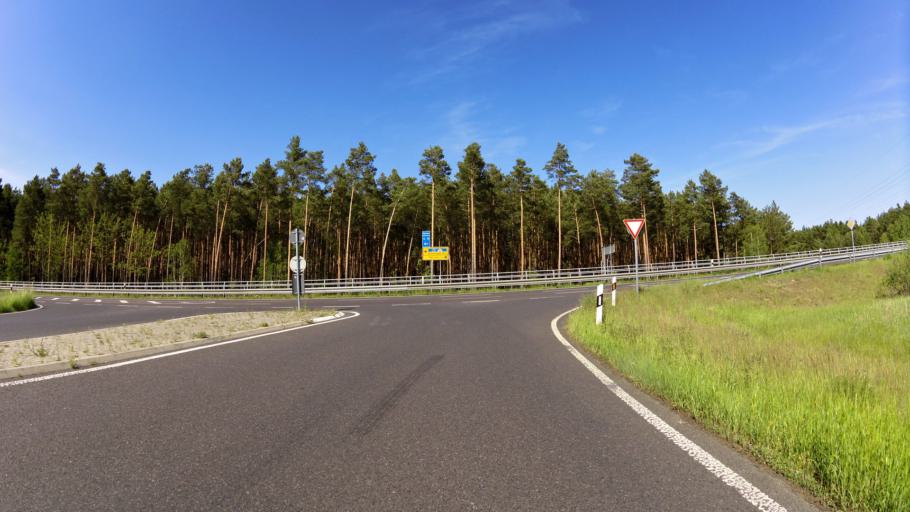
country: DE
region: Brandenburg
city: Mullrose
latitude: 52.2609
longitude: 14.4070
